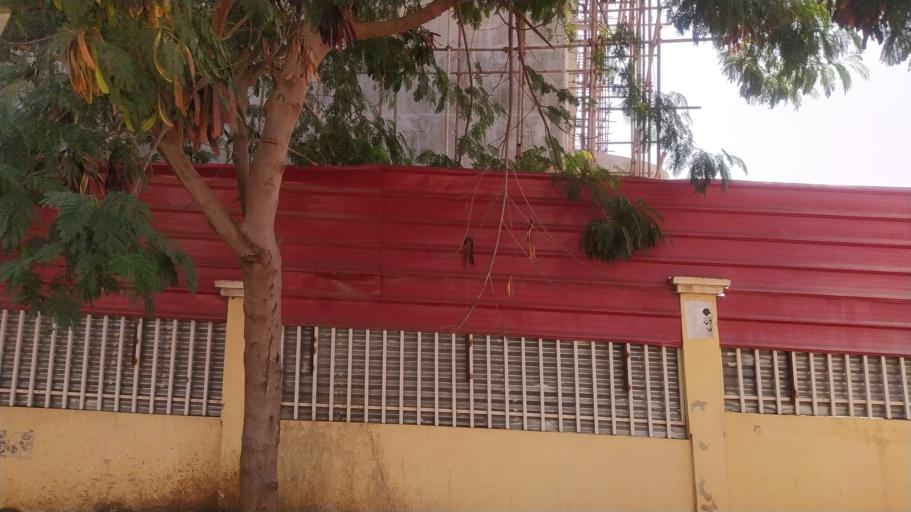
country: AO
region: Luanda
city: Luanda
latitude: -8.9026
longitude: 13.2312
